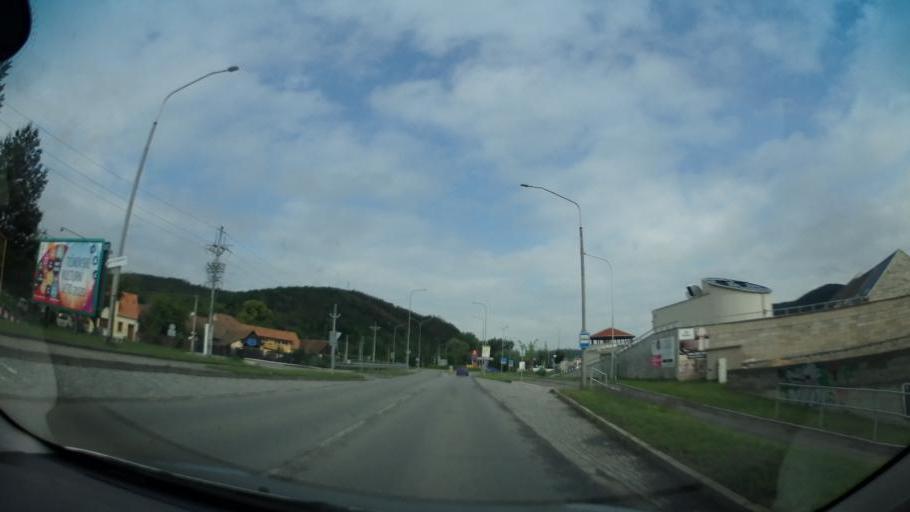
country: CZ
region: South Moravian
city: Tisnov
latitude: 49.3408
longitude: 16.4202
